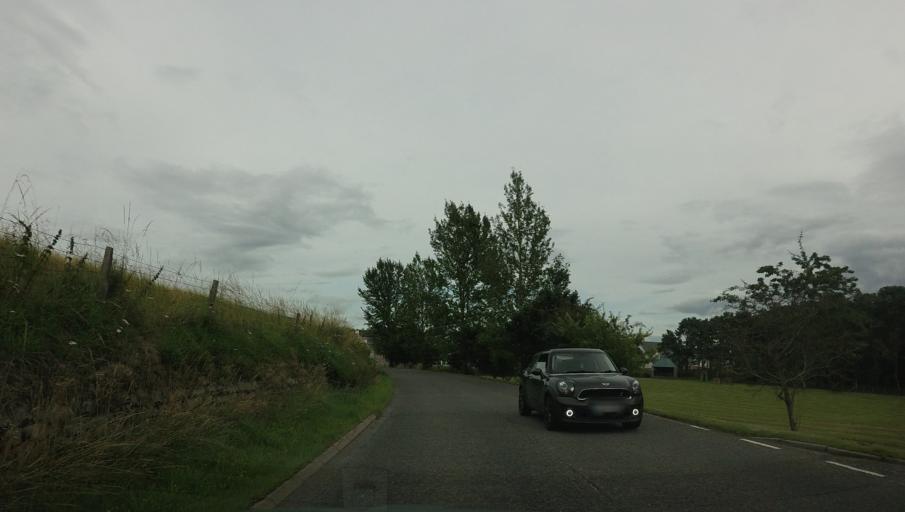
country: GB
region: Scotland
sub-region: Aberdeenshire
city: Torphins
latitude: 57.0866
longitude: -2.6830
